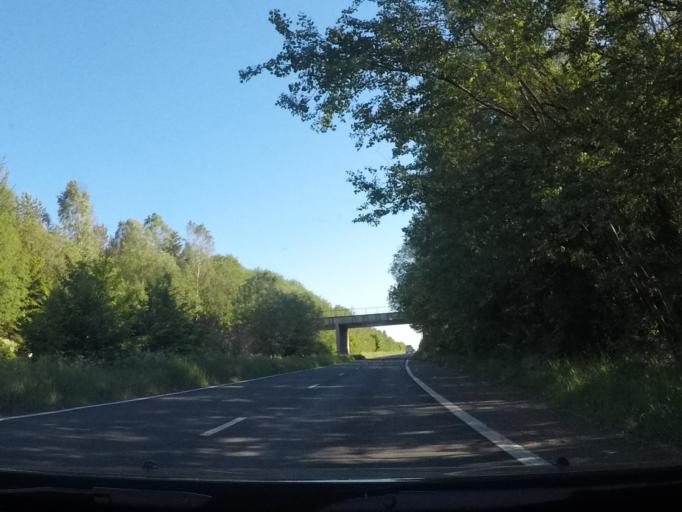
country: BE
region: Wallonia
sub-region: Province du Luxembourg
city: Saint-Hubert
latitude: 49.9893
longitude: 5.3798
